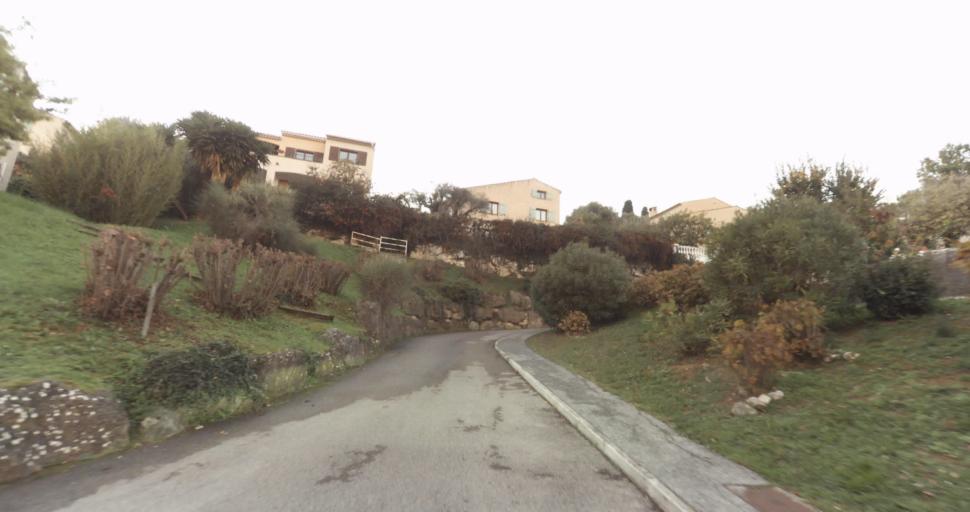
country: FR
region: Provence-Alpes-Cote d'Azur
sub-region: Departement des Alpes-Maritimes
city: Vence
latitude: 43.7214
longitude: 7.1258
